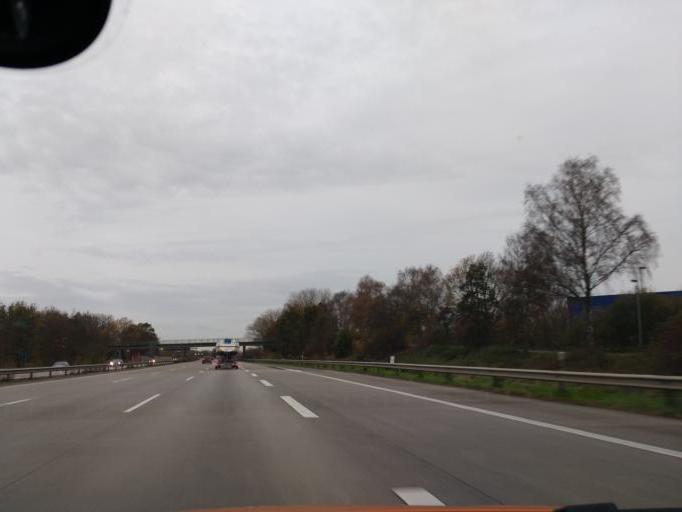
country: DE
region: Lower Saxony
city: Stuhr
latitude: 53.0230
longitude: 8.7982
